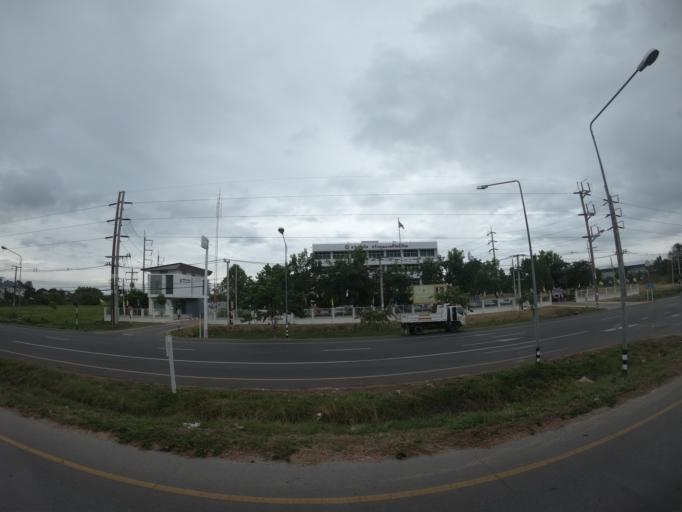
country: TH
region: Roi Et
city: Roi Et
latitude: 16.0449
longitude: 103.6266
